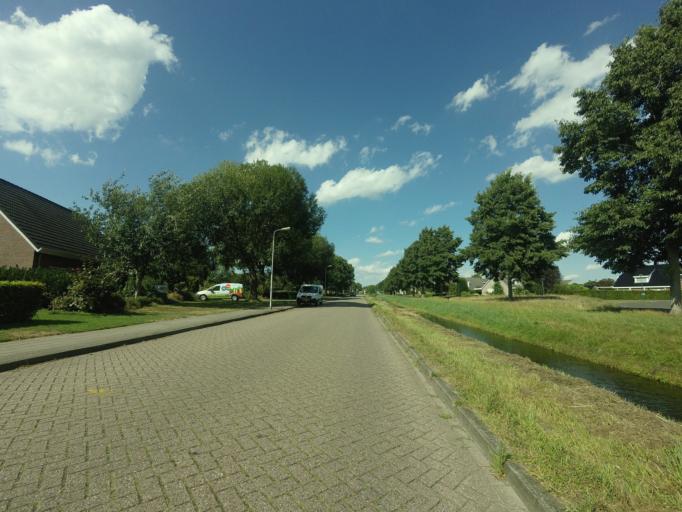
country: NL
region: Drenthe
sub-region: Gemeente Hoogeveen
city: Hoogeveen
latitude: 52.5937
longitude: 6.4605
